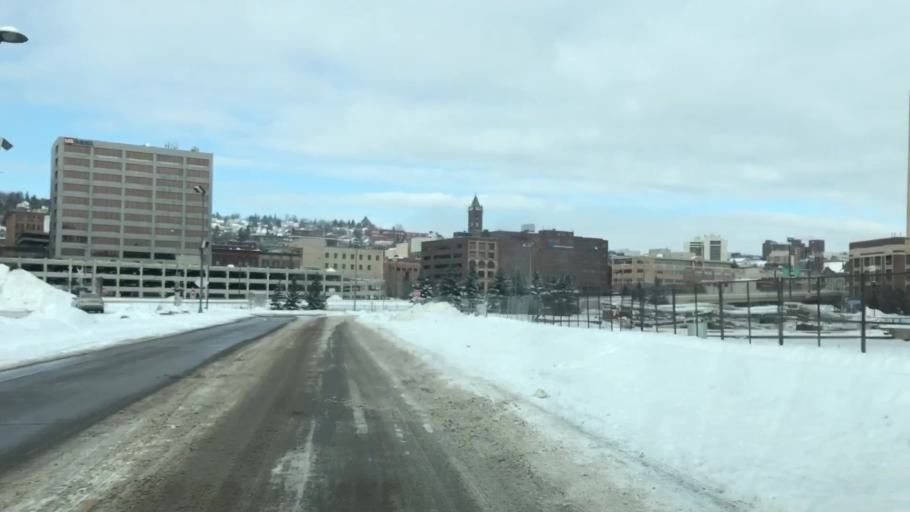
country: US
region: Minnesota
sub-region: Saint Louis County
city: Duluth
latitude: 46.7829
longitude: -92.0978
